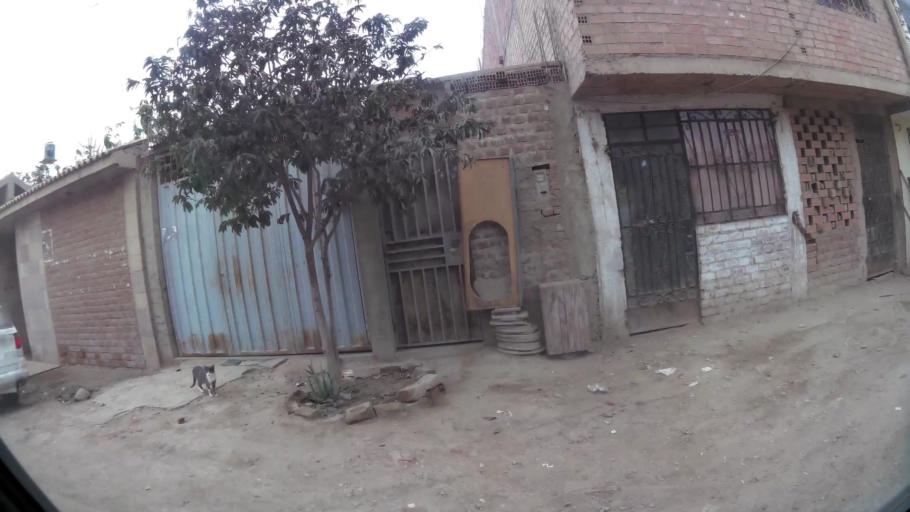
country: PE
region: Lima
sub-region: Lima
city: Independencia
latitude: -11.9637
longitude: -77.0958
